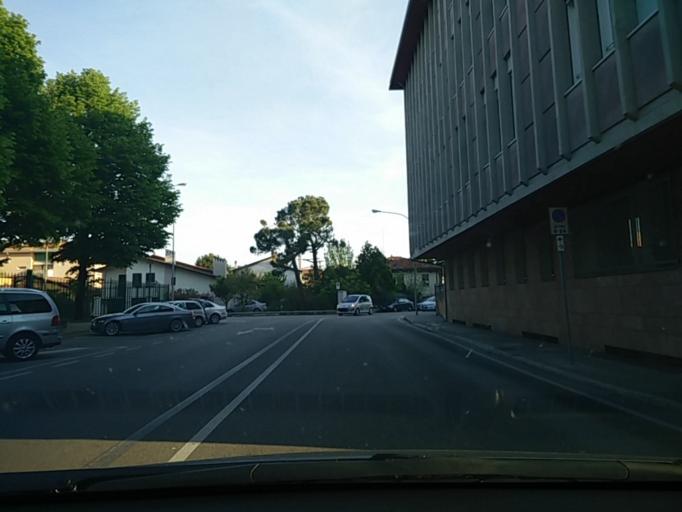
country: IT
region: Veneto
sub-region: Provincia di Venezia
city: San Dona di Piave
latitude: 45.6303
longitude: 12.5733
